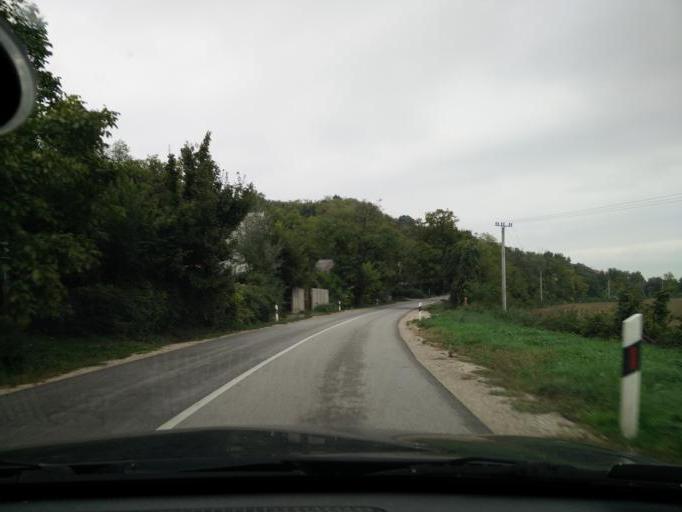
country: HU
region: Komarom-Esztergom
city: Tat
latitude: 47.7188
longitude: 18.6279
